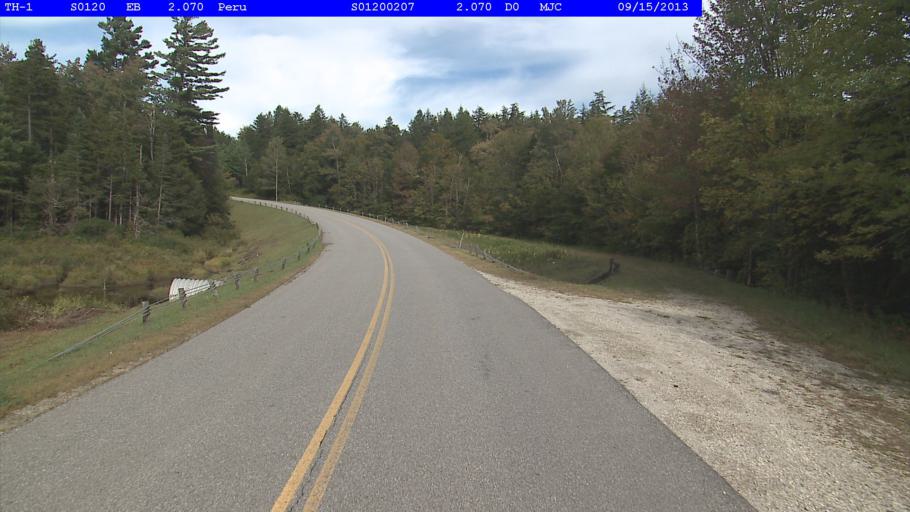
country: US
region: Vermont
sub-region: Bennington County
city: Manchester Center
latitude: 43.2525
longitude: -72.8871
